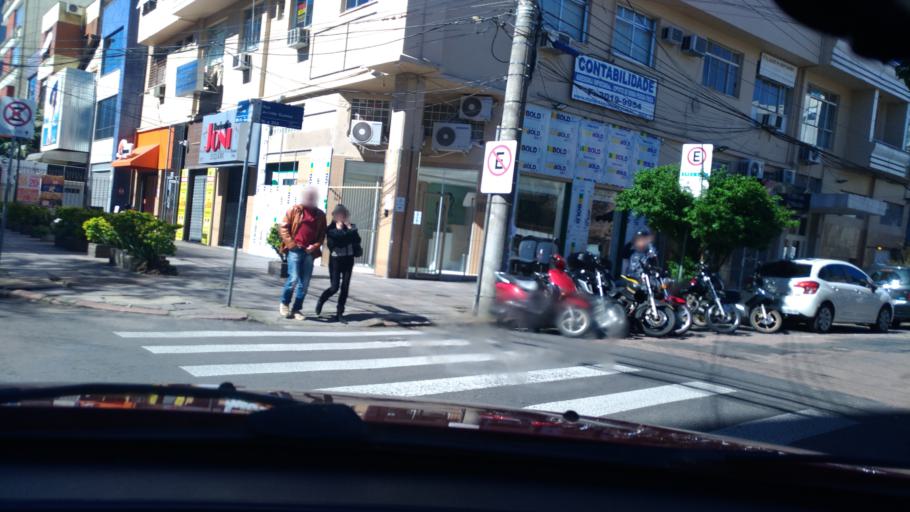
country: BR
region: Rio Grande do Sul
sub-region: Porto Alegre
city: Porto Alegre
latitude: -30.0375
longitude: -51.2101
